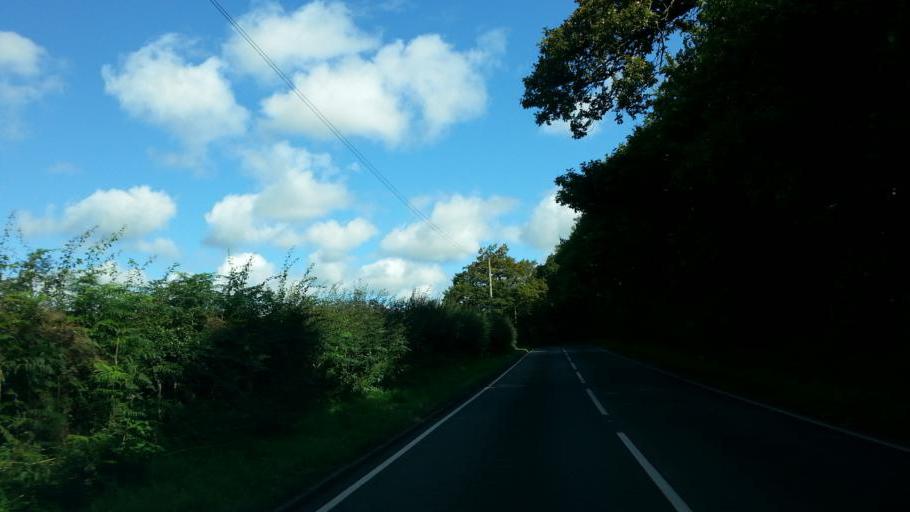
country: GB
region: England
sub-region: Staffordshire
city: Uttoxeter
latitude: 52.8394
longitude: -1.8996
